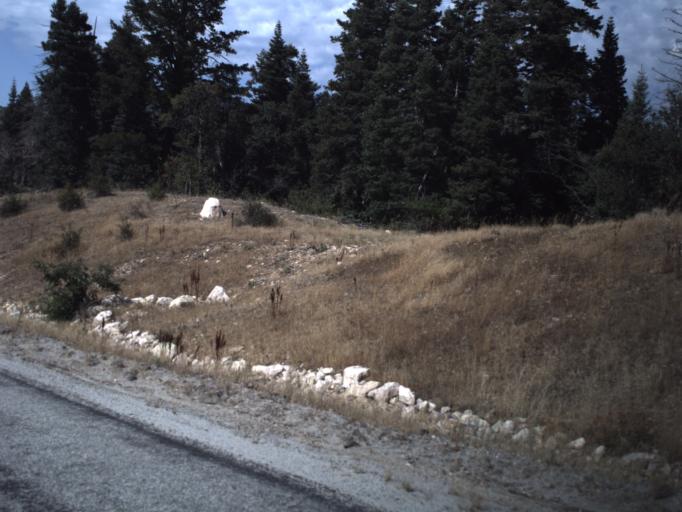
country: US
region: Utah
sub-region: Morgan County
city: Mountain Green
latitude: 41.2200
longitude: -111.8523
